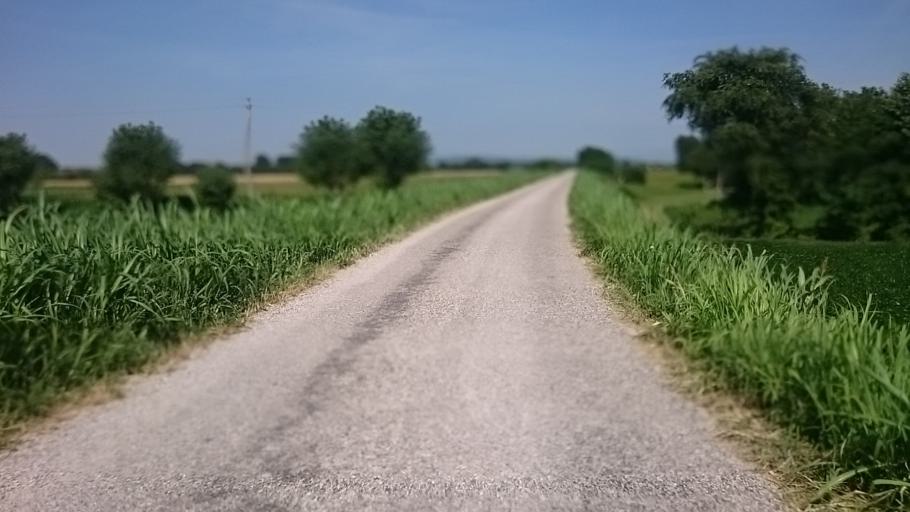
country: IT
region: Veneto
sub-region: Provincia di Padova
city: Selvazzano Dentro
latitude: 45.3987
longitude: 11.7764
